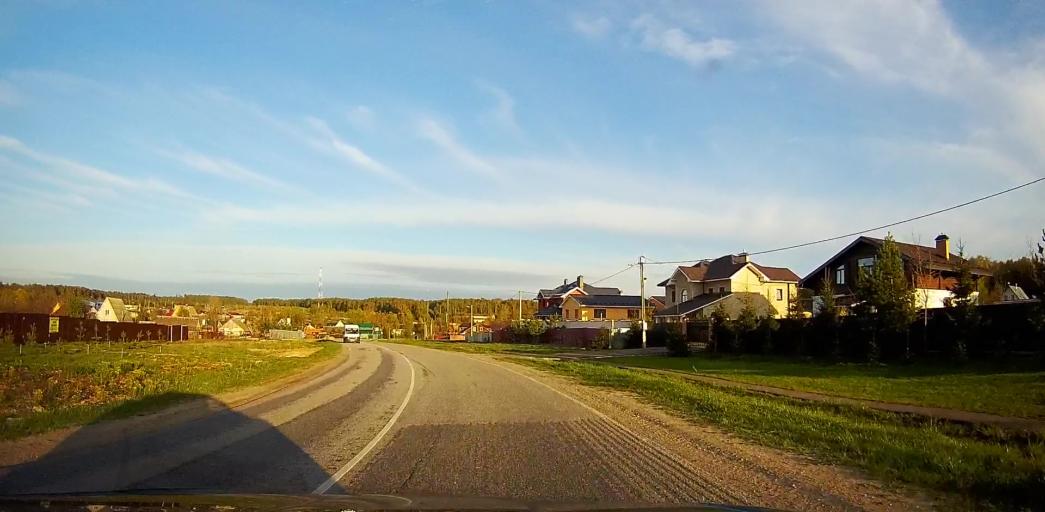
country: RU
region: Moskovskaya
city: Meshcherino
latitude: 55.2325
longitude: 38.3648
